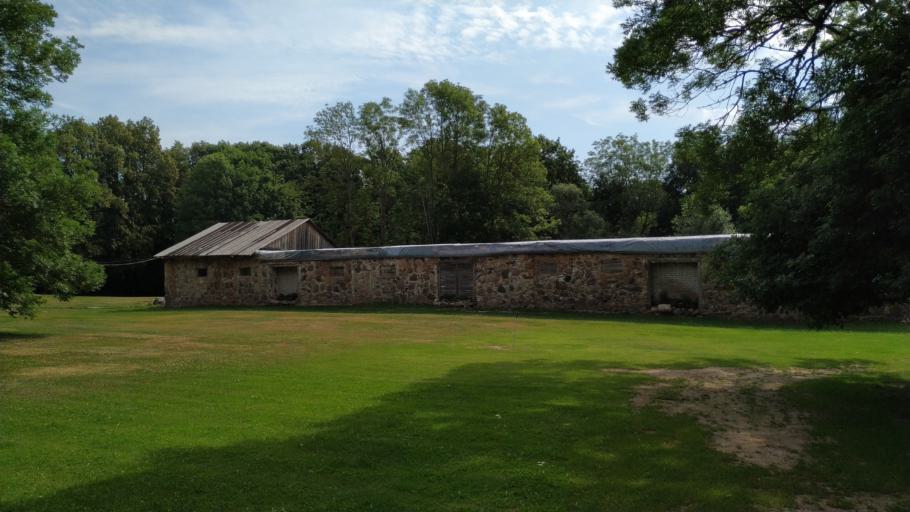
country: LT
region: Panevezys
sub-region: Birzai
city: Birzai
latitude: 56.2150
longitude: 24.6821
